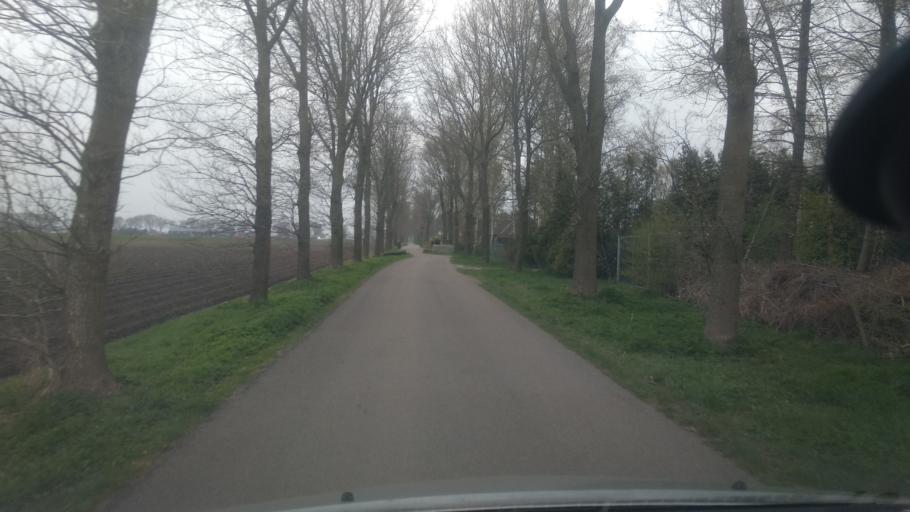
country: NL
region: Groningen
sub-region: Gemeente Stadskanaal
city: Stadskanaal
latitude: 52.9442
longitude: 6.9943
